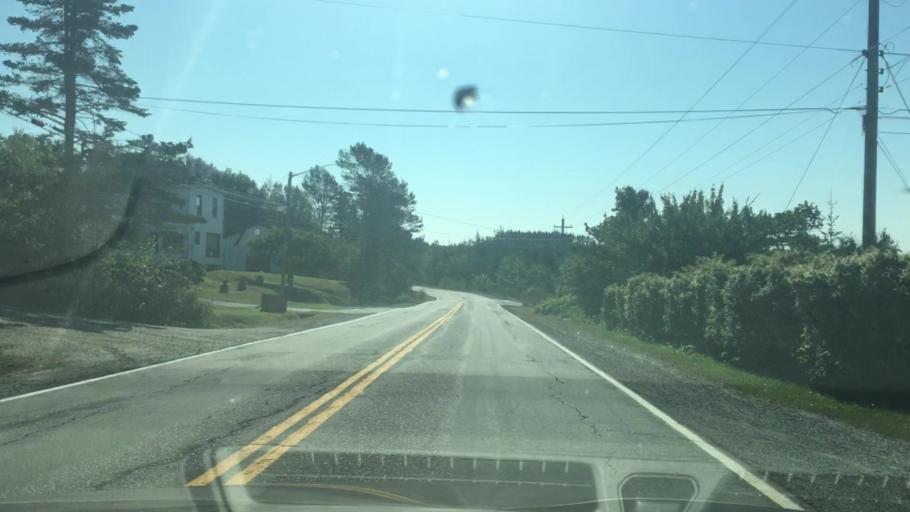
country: CA
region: Nova Scotia
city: Cole Harbour
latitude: 44.7763
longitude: -63.0562
